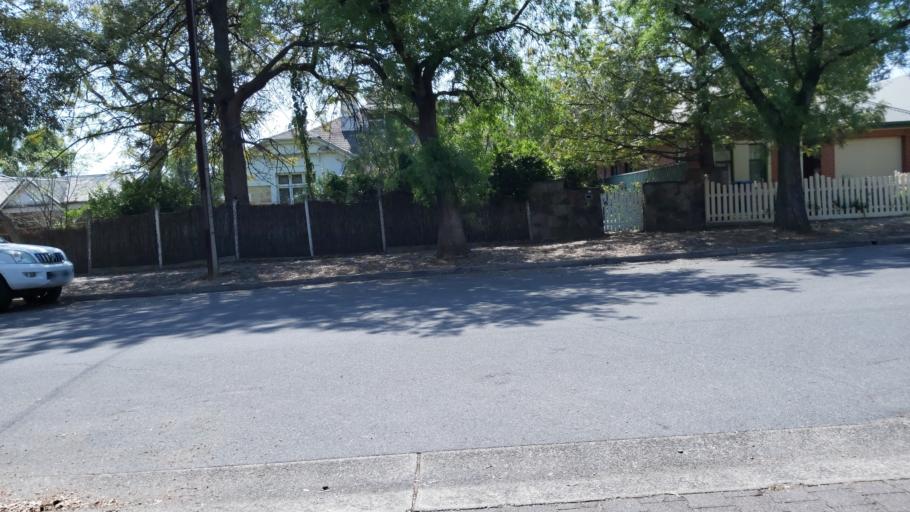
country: AU
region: South Australia
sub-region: Unley
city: Fullarton
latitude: -34.9508
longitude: 138.6280
